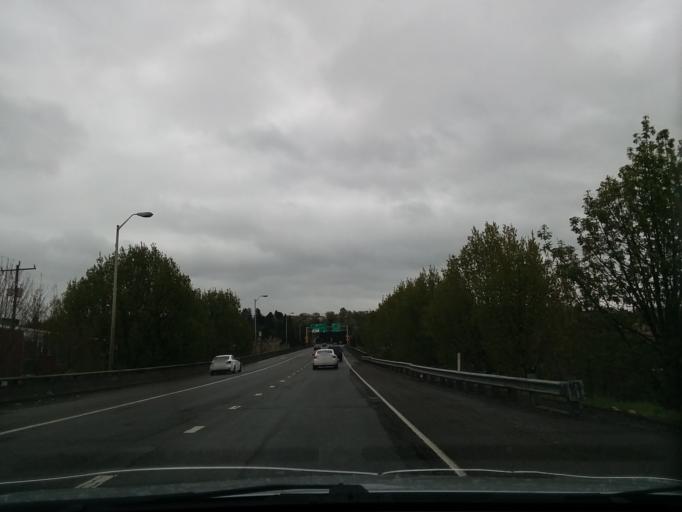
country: US
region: Washington
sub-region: King County
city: White Center
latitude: 47.5482
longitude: -122.3190
